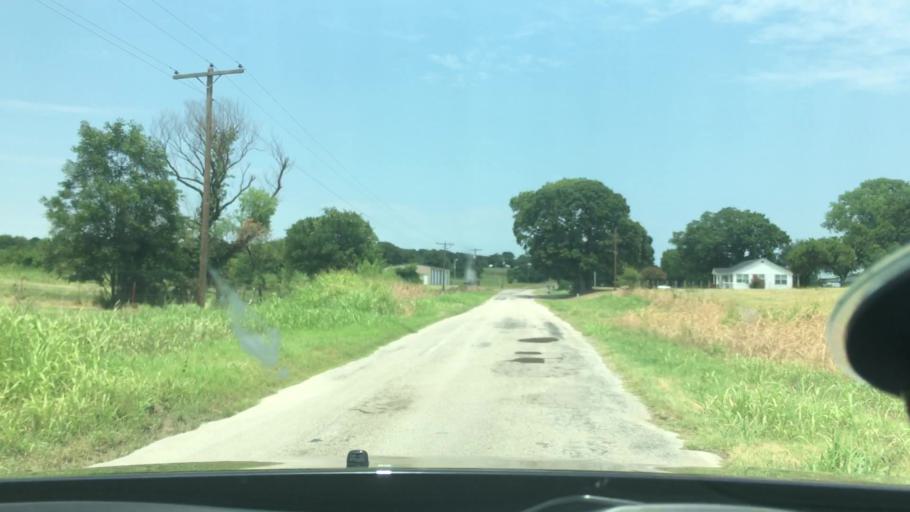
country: US
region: Texas
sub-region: Cooke County
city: Muenster
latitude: 33.8799
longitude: -97.3565
